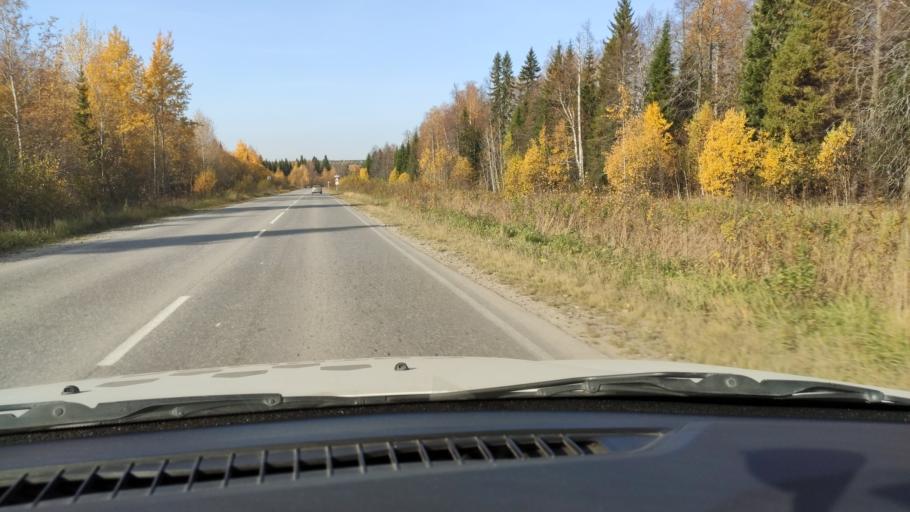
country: RU
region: Perm
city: Novyye Lyady
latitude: 58.0368
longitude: 56.6012
